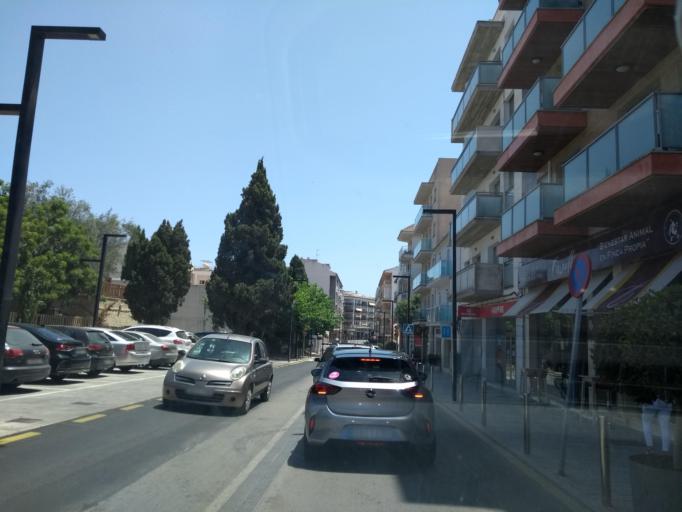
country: ES
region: Balearic Islands
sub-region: Illes Balears
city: Port d'Alcudia
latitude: 39.8421
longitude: 3.1352
